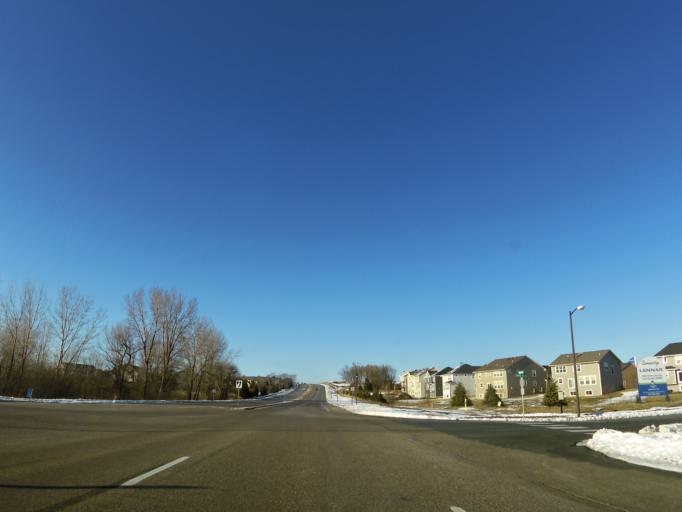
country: US
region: Minnesota
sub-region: Dakota County
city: Lakeville
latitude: 44.6665
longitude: -93.2525
